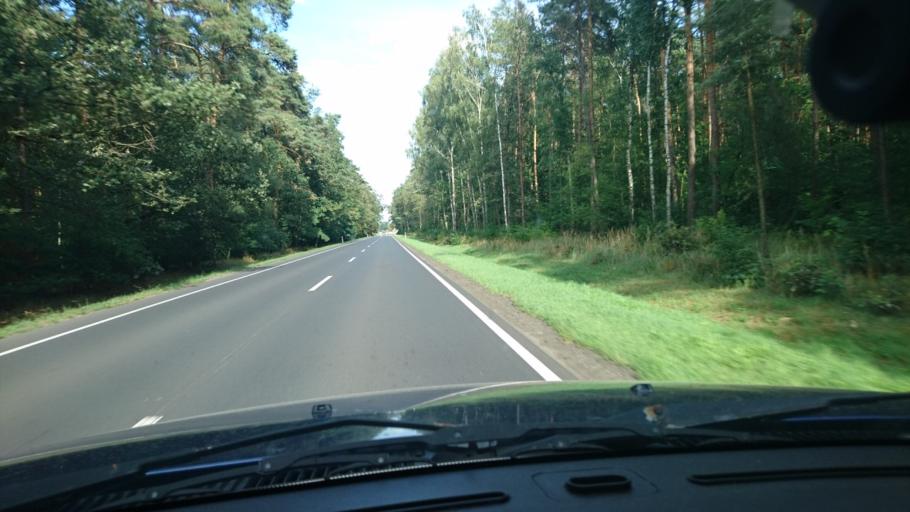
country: PL
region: Greater Poland Voivodeship
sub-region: Powiat krotoszynski
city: Kobylin
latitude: 51.7089
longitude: 17.1959
